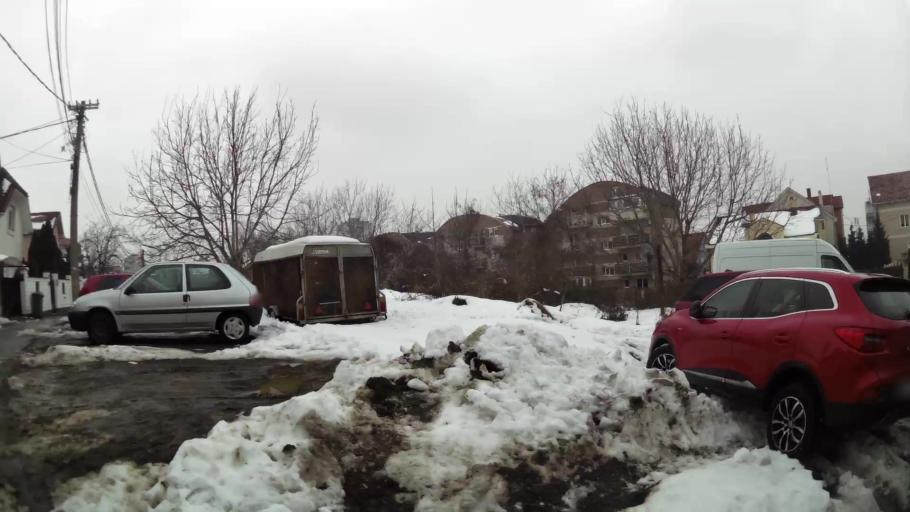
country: RS
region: Central Serbia
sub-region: Belgrade
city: Zvezdara
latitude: 44.7690
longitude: 20.5035
